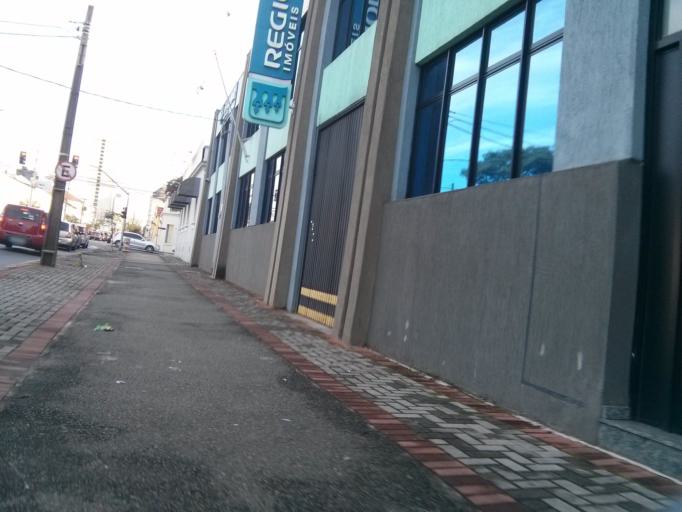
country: BR
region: Parana
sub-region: Curitiba
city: Curitiba
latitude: -25.4447
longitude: -49.2697
